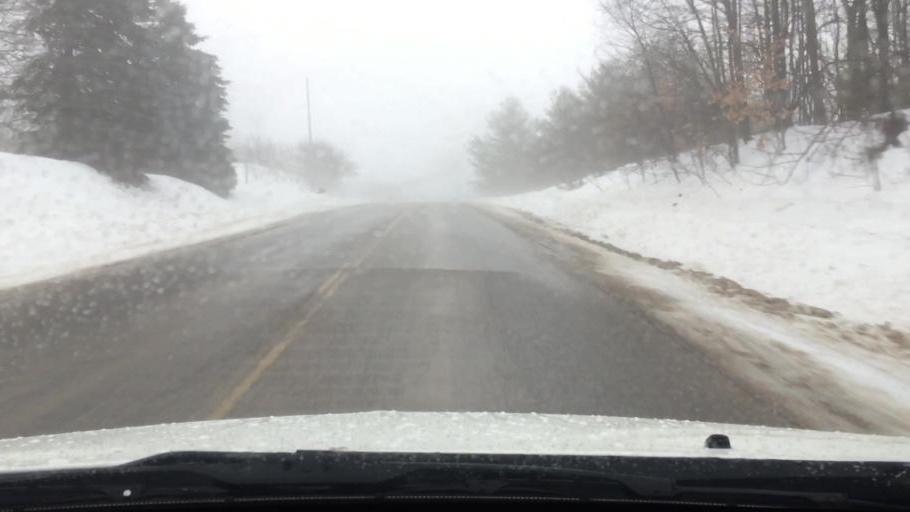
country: US
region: Michigan
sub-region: Charlevoix County
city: East Jordan
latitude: 45.1250
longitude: -85.1802
